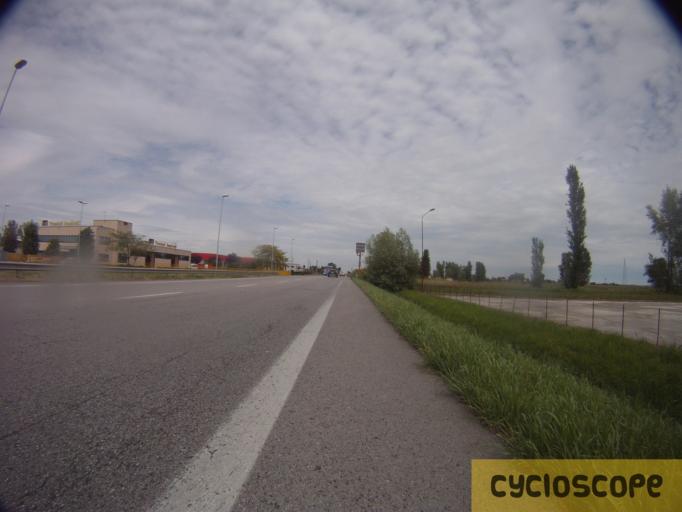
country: IT
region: Veneto
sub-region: Provincia di Rovigo
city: Porto Viro
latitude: 45.0415
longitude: 12.2426
